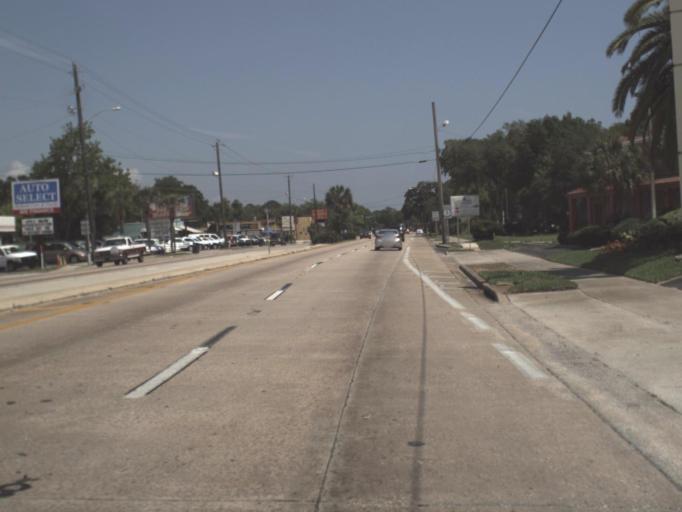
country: US
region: Florida
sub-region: Saint Johns County
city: Saint Augustine
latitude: 29.9170
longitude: -81.3245
